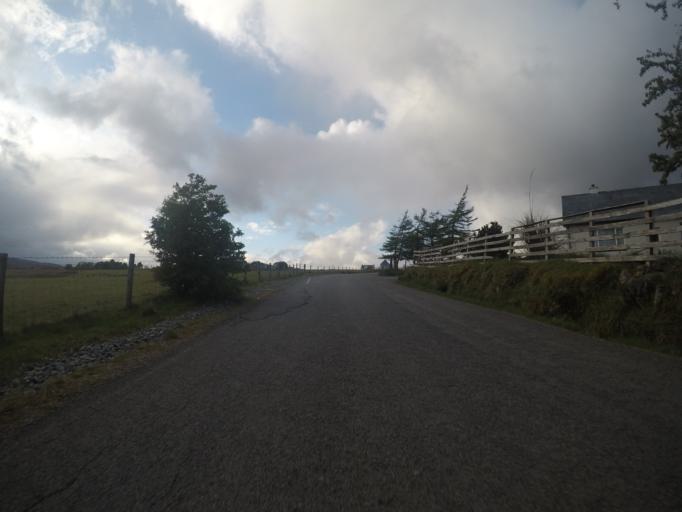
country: GB
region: Scotland
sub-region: Highland
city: Isle of Skye
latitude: 57.4549
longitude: -6.2979
